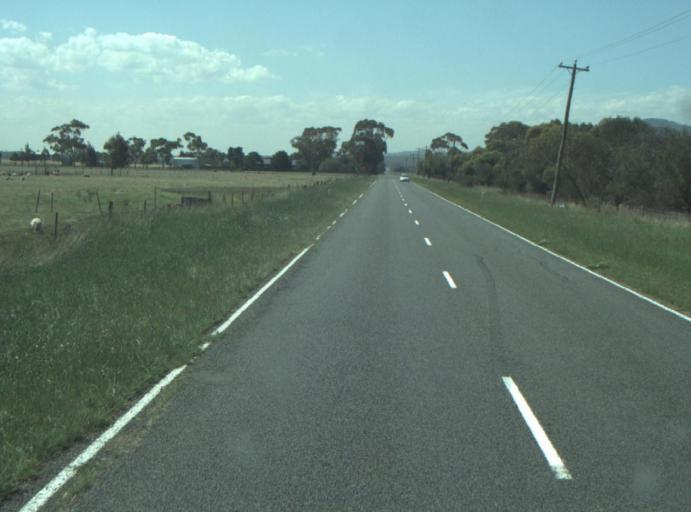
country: AU
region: Victoria
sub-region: Greater Geelong
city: Lara
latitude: -37.9971
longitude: 144.4009
